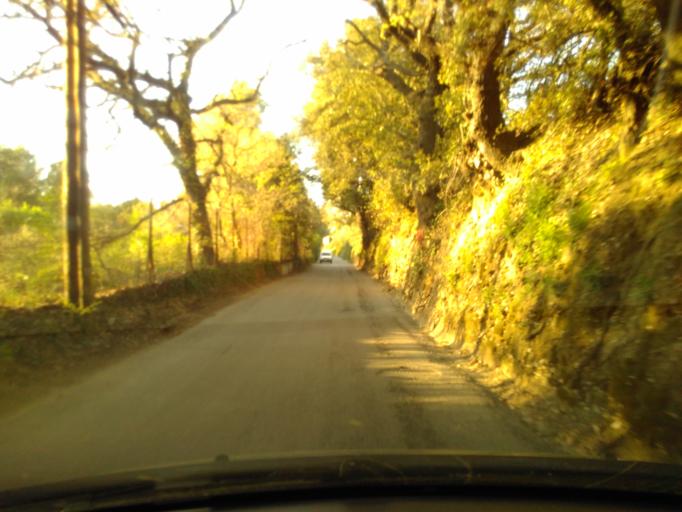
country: FR
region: Provence-Alpes-Cote d'Azur
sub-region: Departement du Vaucluse
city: Carpentras
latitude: 44.0546
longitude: 5.0703
